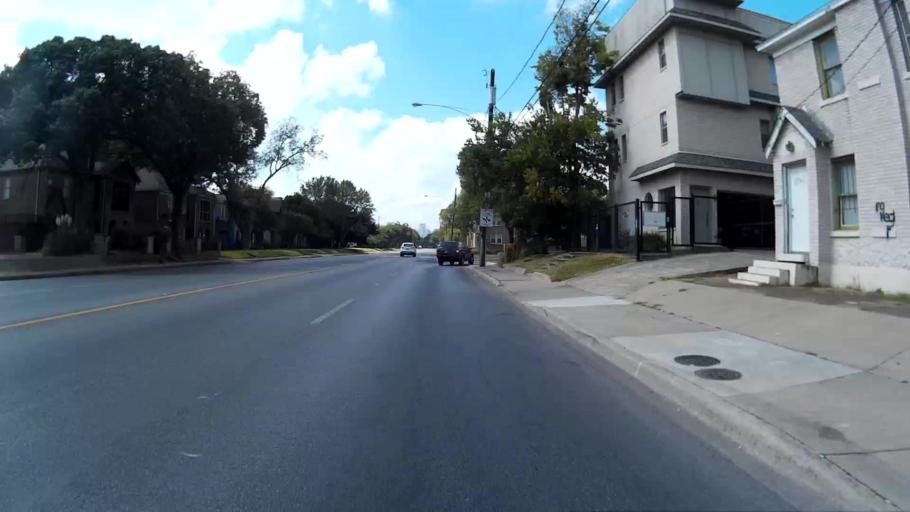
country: US
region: Texas
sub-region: Dallas County
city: Highland Park
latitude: 32.8115
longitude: -96.7625
